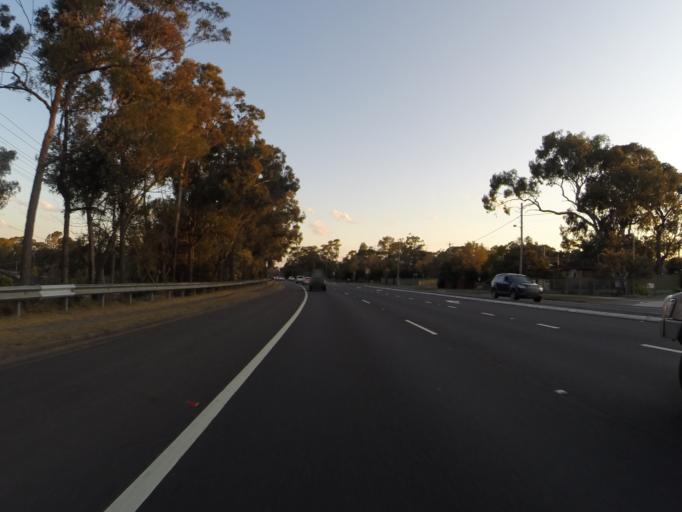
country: AU
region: New South Wales
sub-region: Blue Mountains Municipality
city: Blaxland
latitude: -33.7503
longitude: 150.6121
